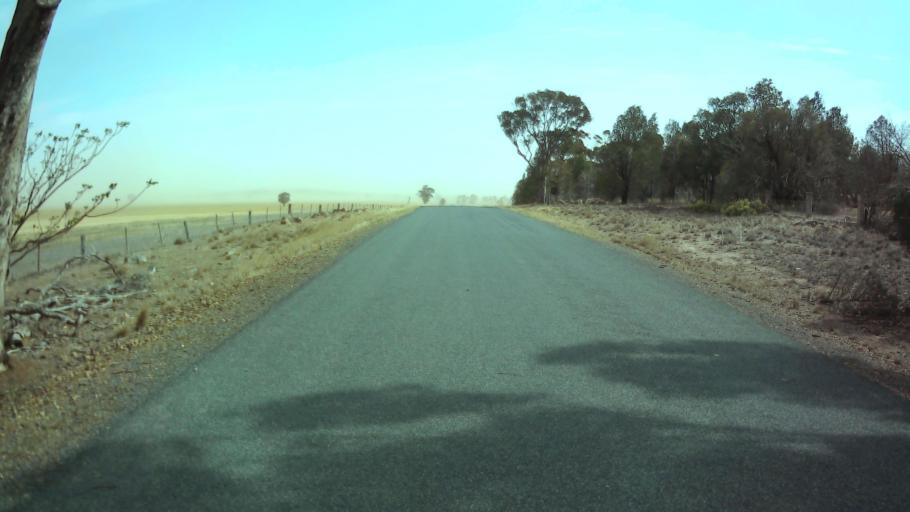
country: AU
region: New South Wales
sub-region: Weddin
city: Grenfell
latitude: -33.7465
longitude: 147.9916
